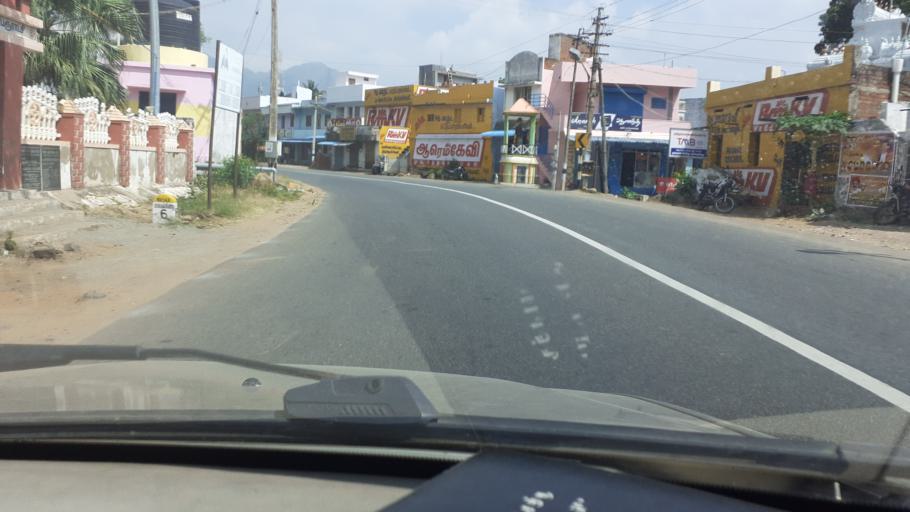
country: IN
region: Tamil Nadu
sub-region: Kanniyakumari
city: Suchindram
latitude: 8.2472
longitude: 77.5208
